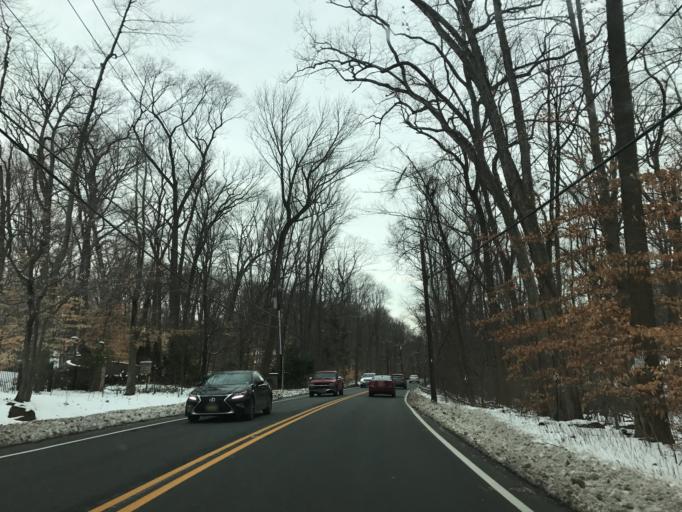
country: US
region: New Jersey
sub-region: Mercer County
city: Princeton
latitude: 40.3783
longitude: -74.6634
